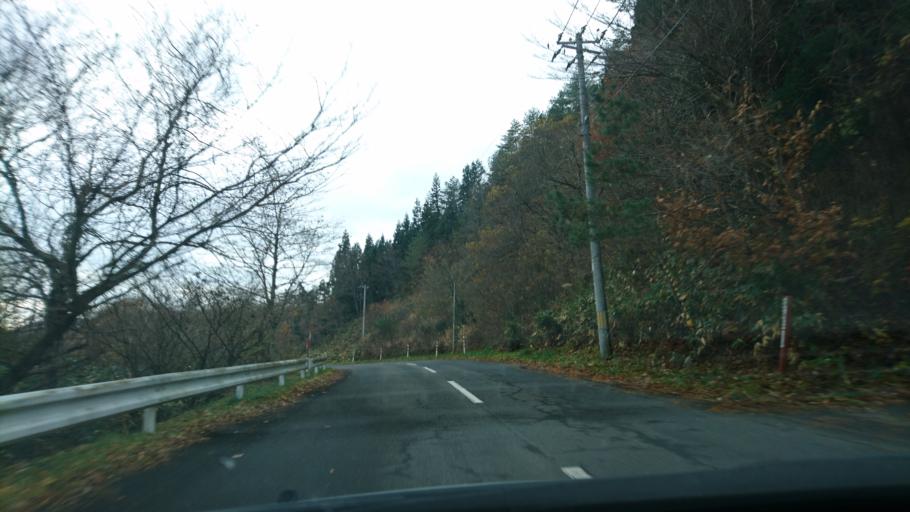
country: JP
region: Iwate
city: Ichinoseki
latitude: 38.9304
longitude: 140.9222
